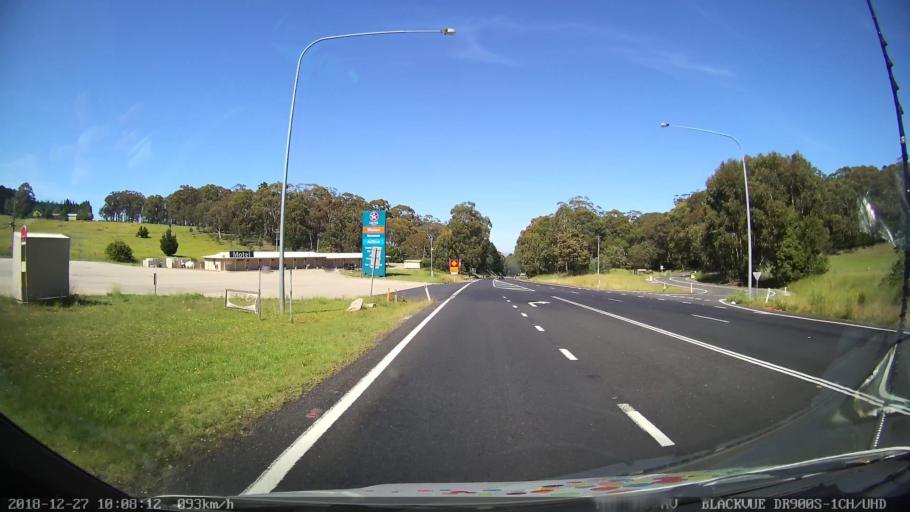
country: AU
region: New South Wales
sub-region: Lithgow
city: Portland
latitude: -33.4462
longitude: 149.8294
